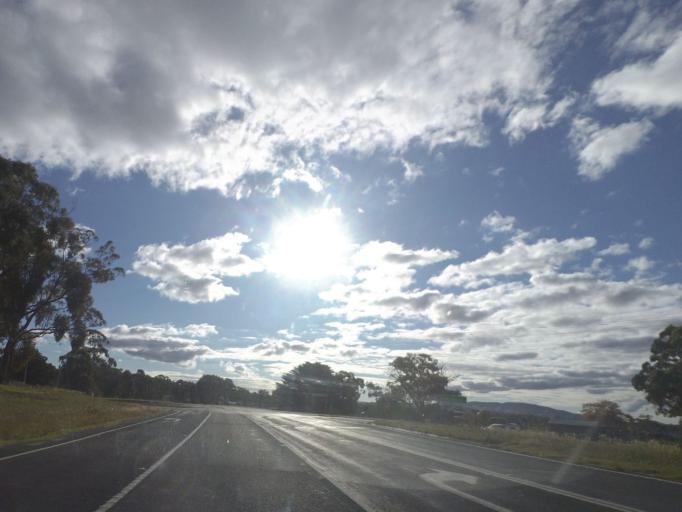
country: AU
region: Victoria
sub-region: Mount Alexander
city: Castlemaine
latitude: -37.1006
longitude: 144.3343
